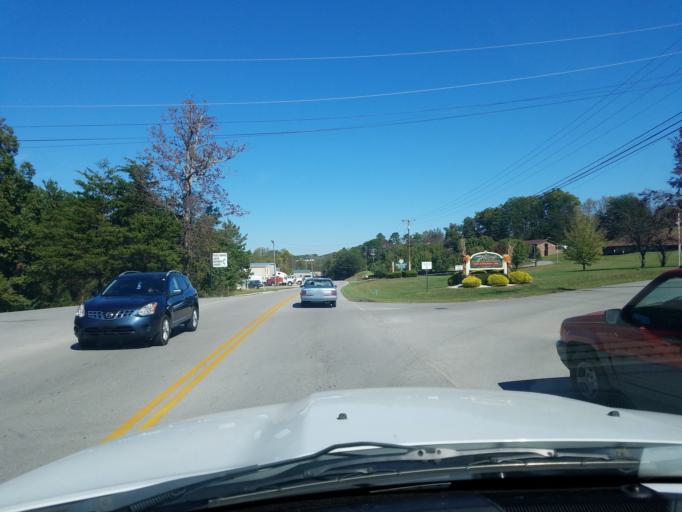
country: US
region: Kentucky
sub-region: Laurel County
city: North Corbin
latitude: 36.9753
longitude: -84.0906
